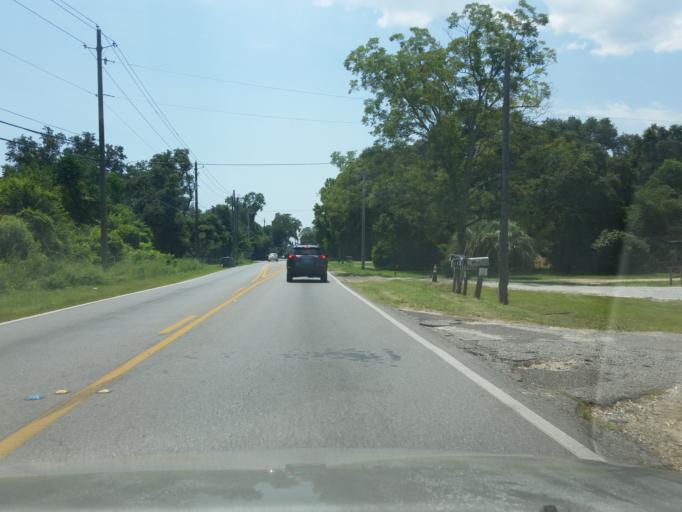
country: US
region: Florida
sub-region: Escambia County
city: Ensley
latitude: 30.4997
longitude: -87.2563
